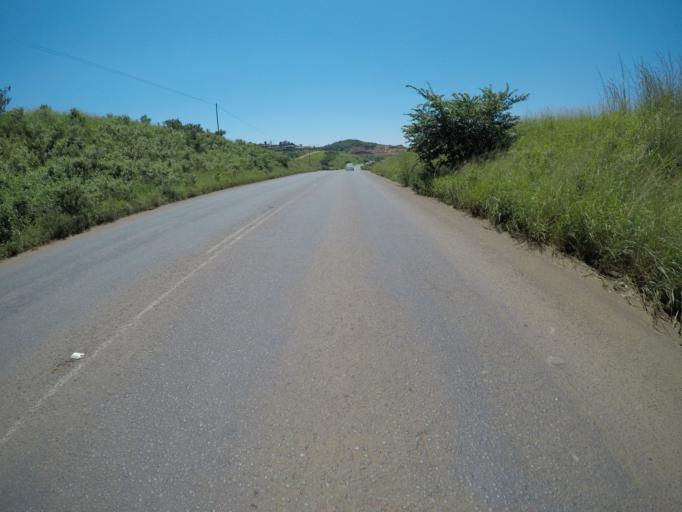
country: ZA
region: KwaZulu-Natal
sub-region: uThungulu District Municipality
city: Empangeni
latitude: -28.7612
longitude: 31.8748
